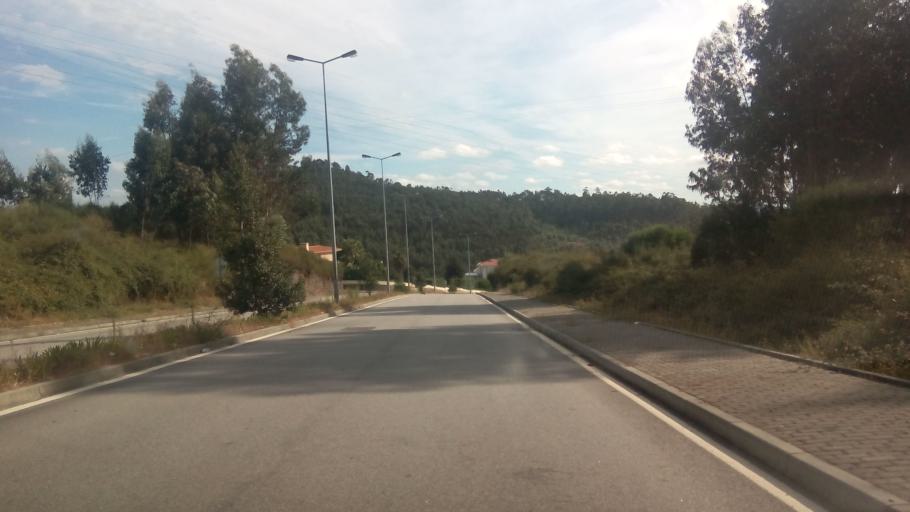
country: PT
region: Porto
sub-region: Paredes
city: Baltar
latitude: 41.1933
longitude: -8.4030
